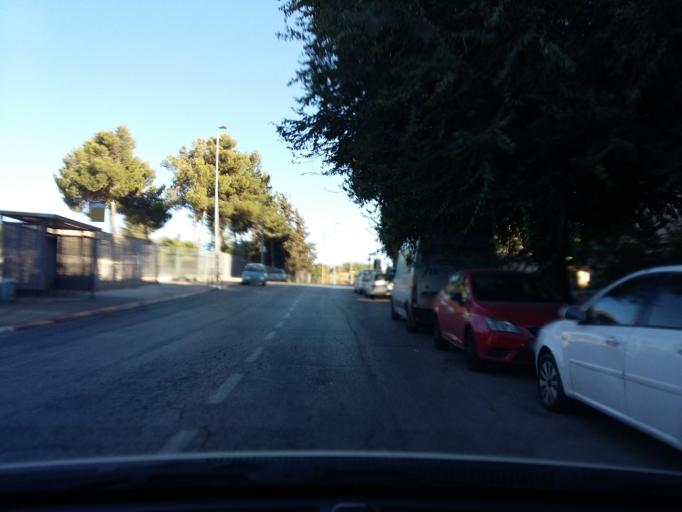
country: PS
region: West Bank
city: East Jerusalem
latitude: 31.8018
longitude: 35.2397
